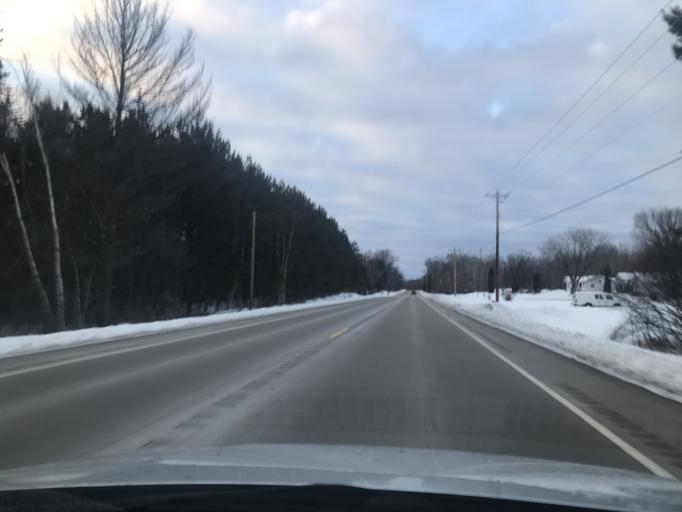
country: US
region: Wisconsin
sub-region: Marinette County
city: Marinette
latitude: 45.1478
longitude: -87.7008
